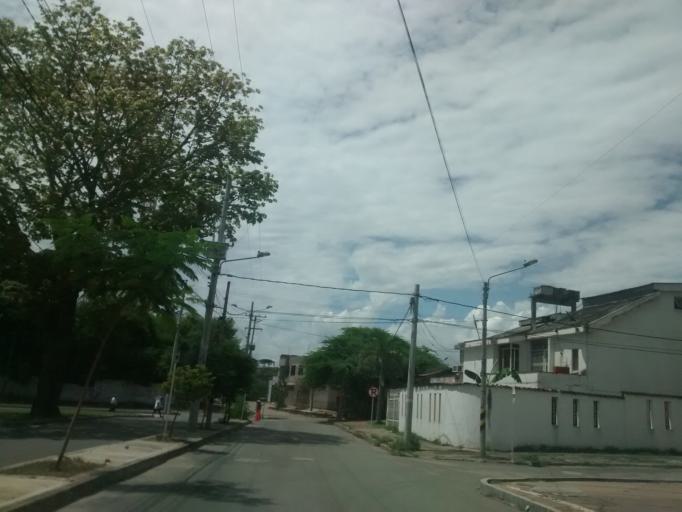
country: CO
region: Cundinamarca
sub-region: Girardot
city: Girardot City
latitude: 4.3069
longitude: -74.7982
